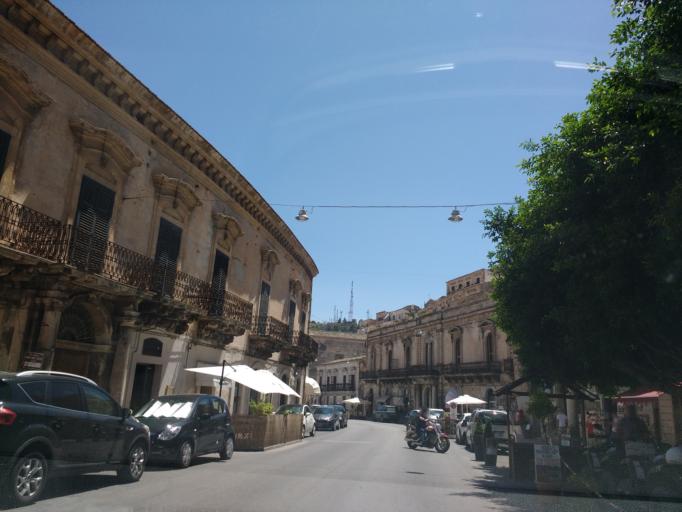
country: IT
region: Sicily
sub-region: Ragusa
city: Modica
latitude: 36.8612
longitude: 14.7599
